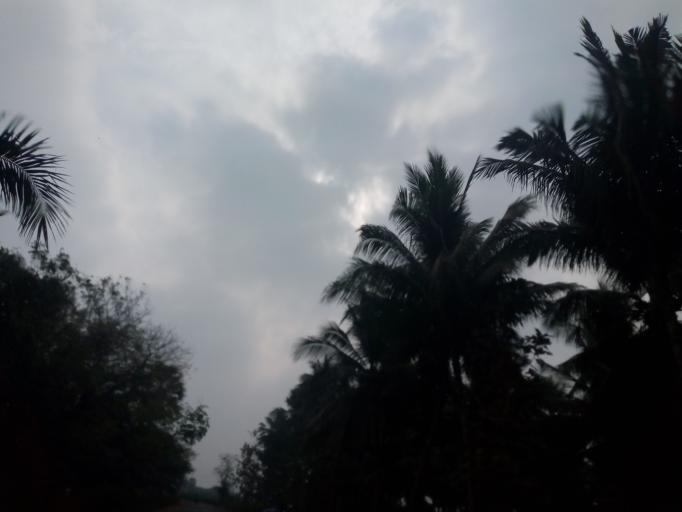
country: IN
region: Andhra Pradesh
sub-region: West Godavari
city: Tadepallegudem
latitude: 16.8655
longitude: 81.3229
